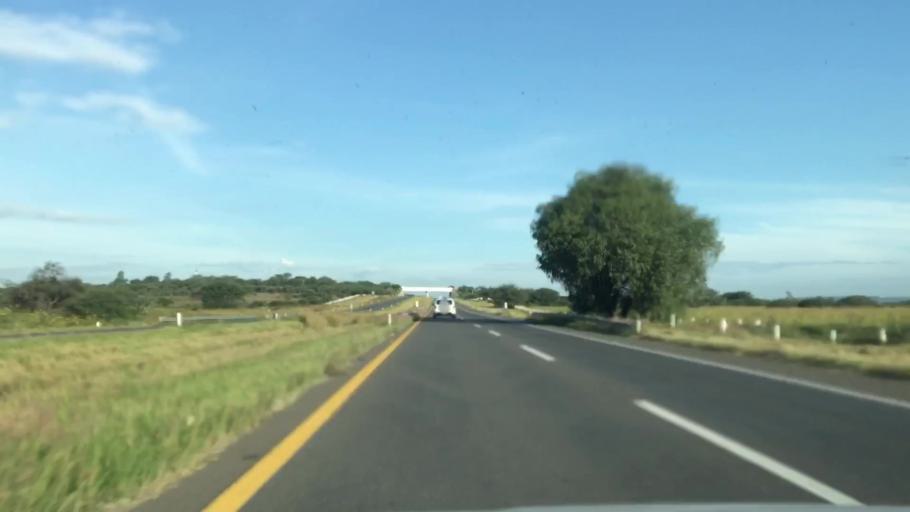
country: MX
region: Jalisco
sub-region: Union de San Antonio
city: San Jose del Caliche (El Caliche)
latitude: 21.1625
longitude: -101.8593
